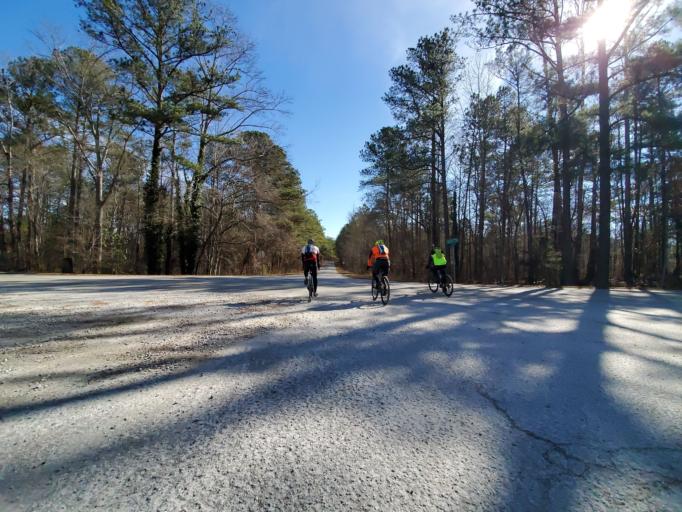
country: US
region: Georgia
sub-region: Fulton County
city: Chattahoochee Hills
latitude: 33.5746
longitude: -84.7770
